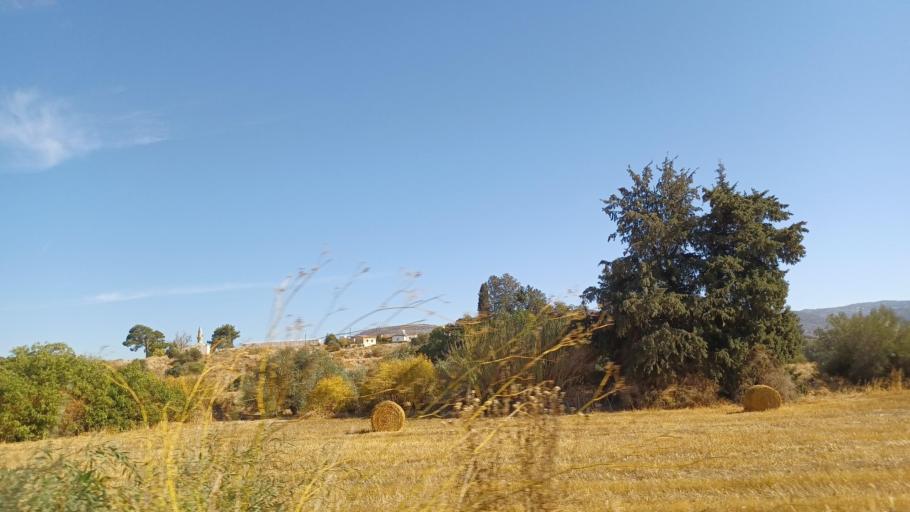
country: CY
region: Pafos
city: Polis
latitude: 35.0029
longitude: 32.4349
